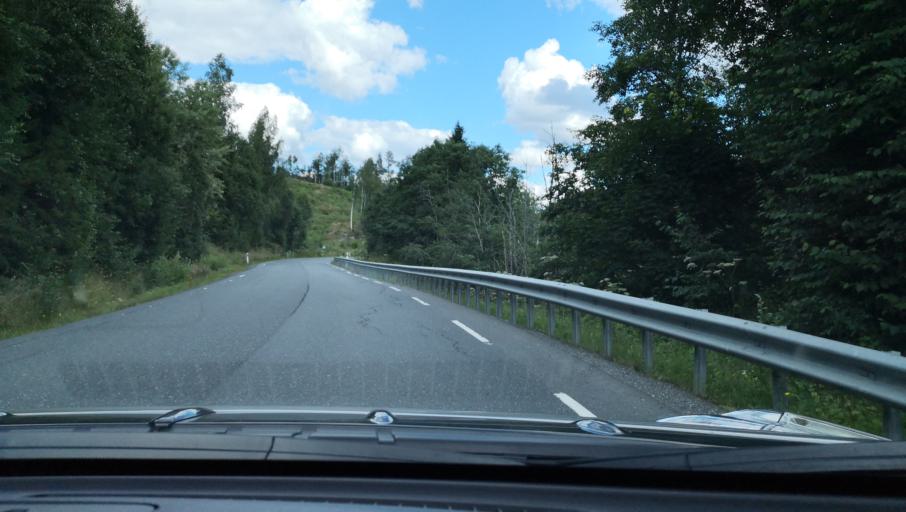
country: NO
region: Ostfold
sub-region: Hobol
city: Tomter
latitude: 59.6451
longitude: 10.9849
